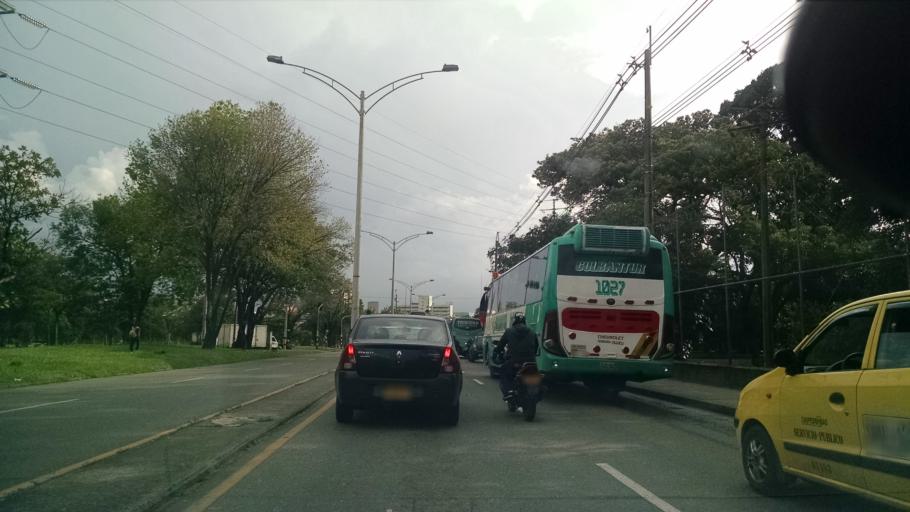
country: CO
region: Antioquia
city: Medellin
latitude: 6.2607
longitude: -75.5751
